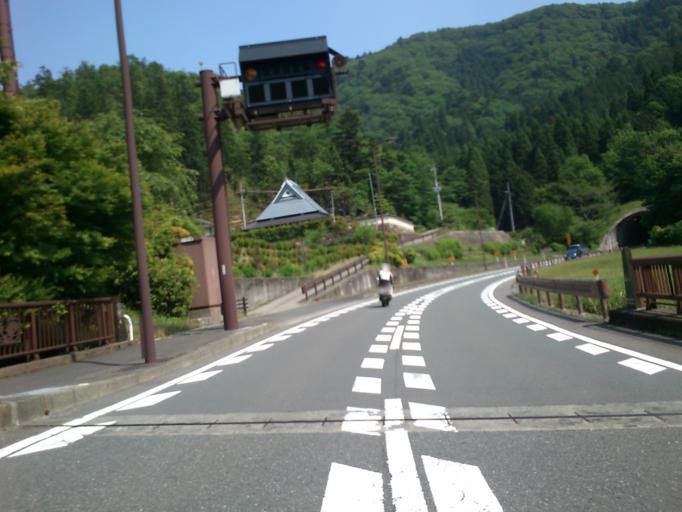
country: JP
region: Kyoto
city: Kameoka
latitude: 35.2312
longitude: 135.5735
